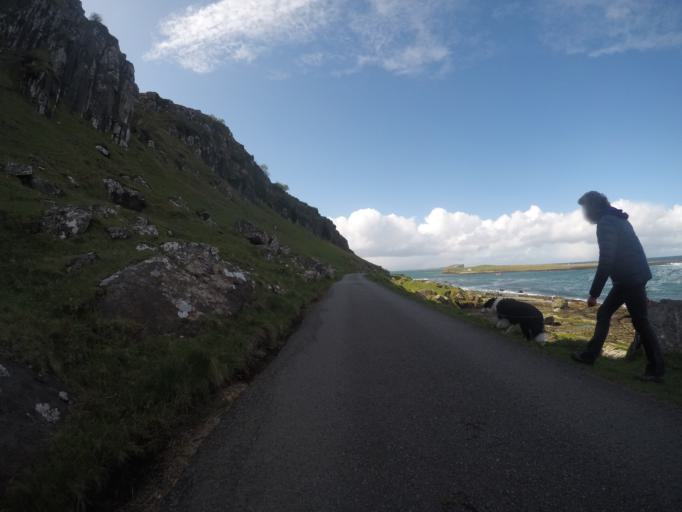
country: GB
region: Scotland
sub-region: Highland
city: Portree
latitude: 57.6343
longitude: -6.2021
